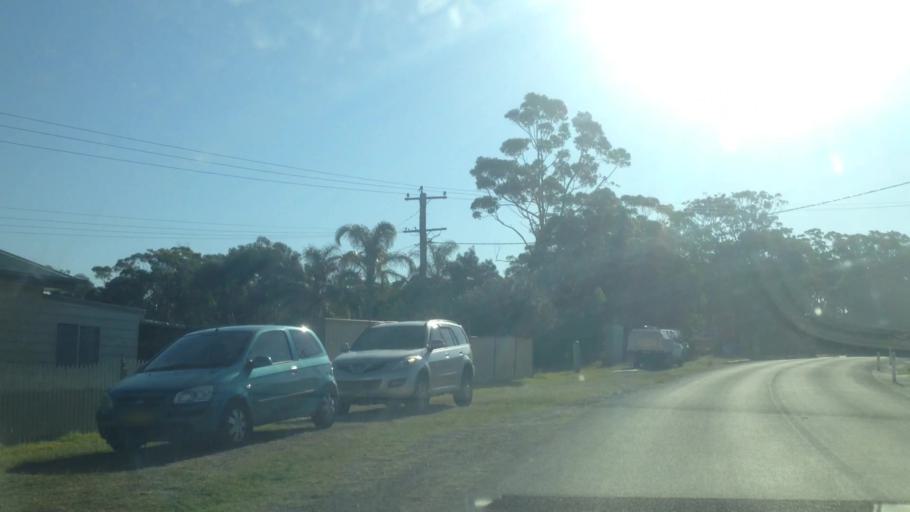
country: AU
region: New South Wales
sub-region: Wyong Shire
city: Kingfisher Shores
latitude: -33.1131
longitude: 151.5635
